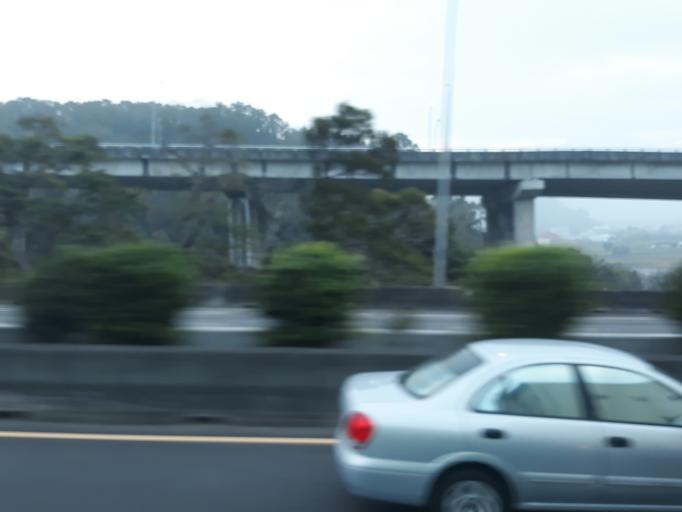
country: TW
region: Taiwan
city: Fengyuan
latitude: 24.3594
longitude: 120.7372
